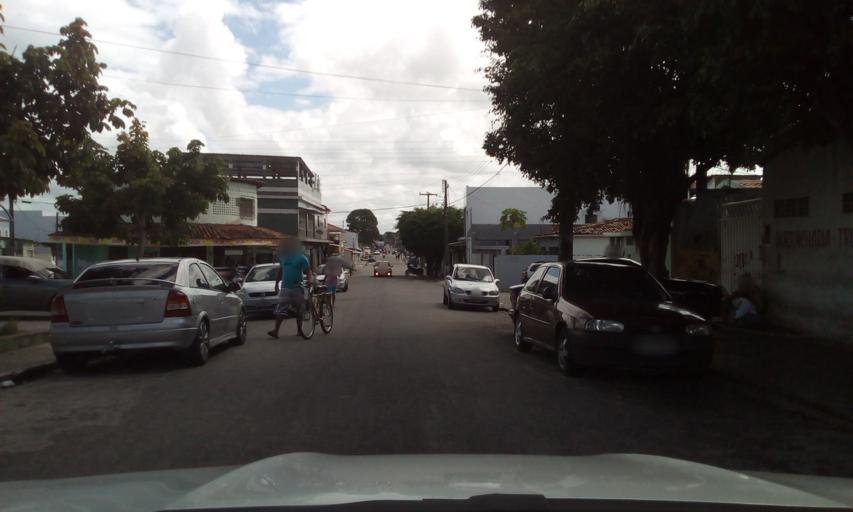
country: BR
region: Paraiba
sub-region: Bayeux
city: Bayeux
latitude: -7.1362
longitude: -34.9214
